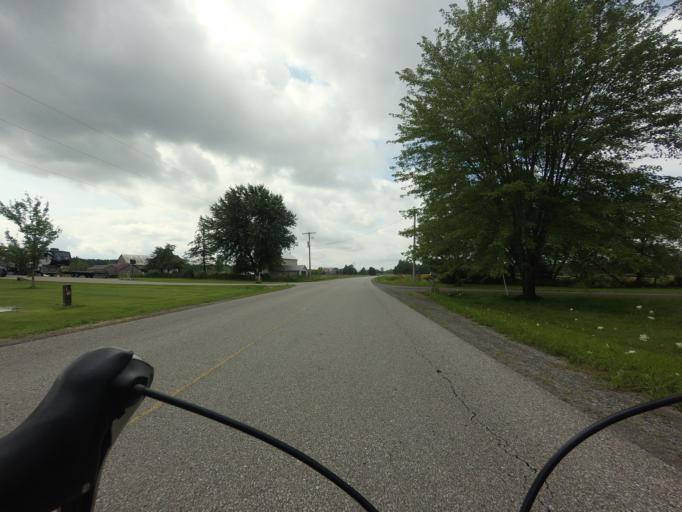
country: CA
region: Ontario
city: Brockville
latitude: 44.7783
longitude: -75.7241
